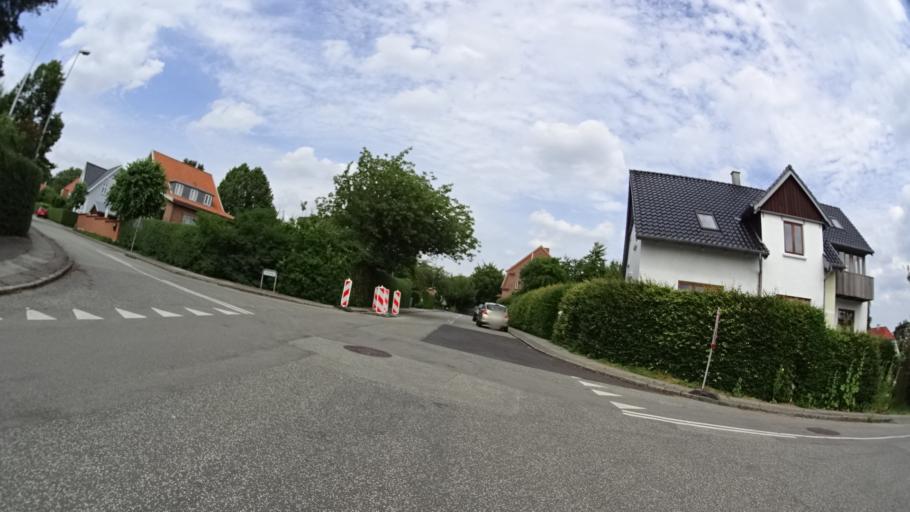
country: DK
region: Central Jutland
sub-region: Arhus Kommune
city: Arhus
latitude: 56.1537
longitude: 10.1729
